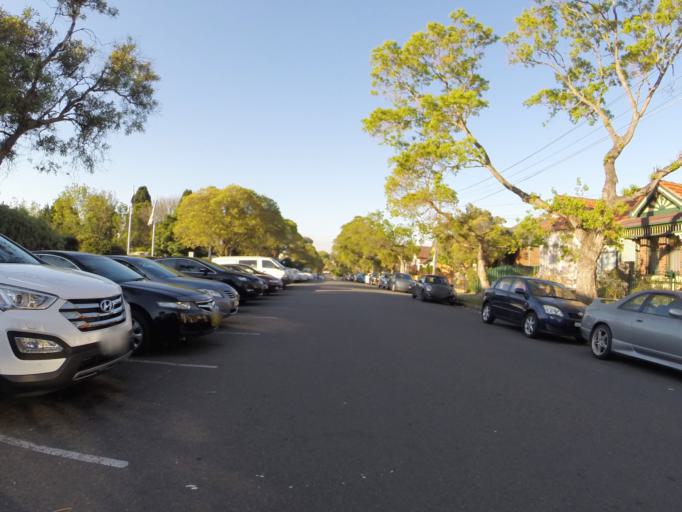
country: AU
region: New South Wales
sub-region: Marrickville
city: Marrickville
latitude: -33.9097
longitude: 151.1559
